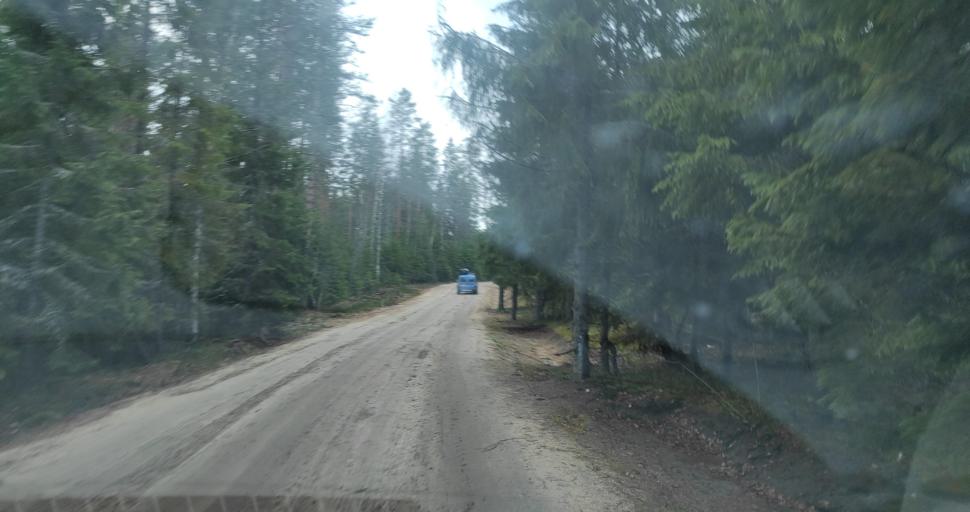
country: RU
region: Republic of Karelia
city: Pitkyaranta
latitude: 61.7524
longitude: 31.4033
